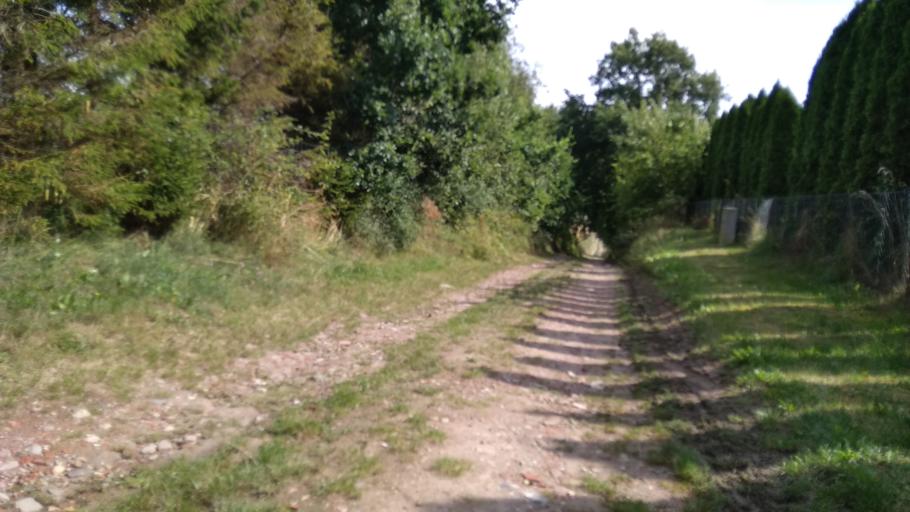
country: PL
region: West Pomeranian Voivodeship
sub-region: Powiat slawienski
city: Darlowo
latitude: 54.5102
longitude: 16.5155
